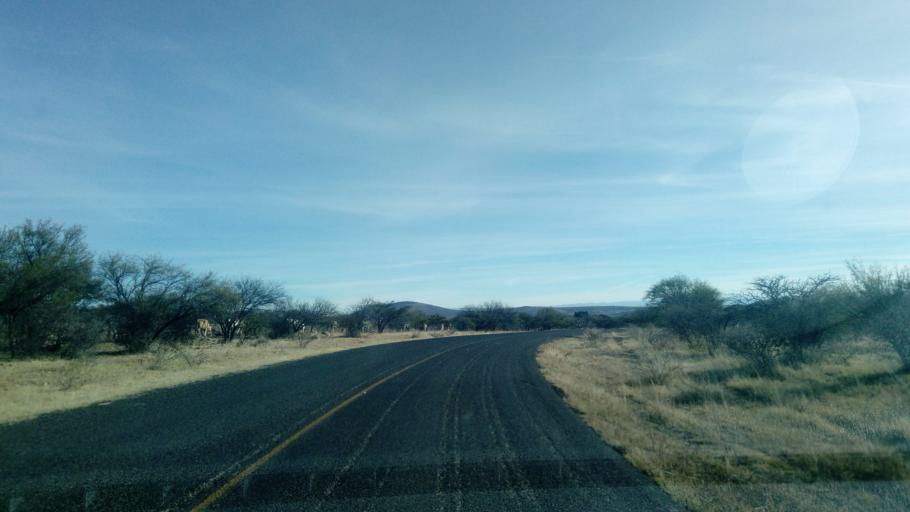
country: MX
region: Durango
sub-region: Nombre de Dios
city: Nombre de Dios
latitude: 23.9411
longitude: -104.3227
